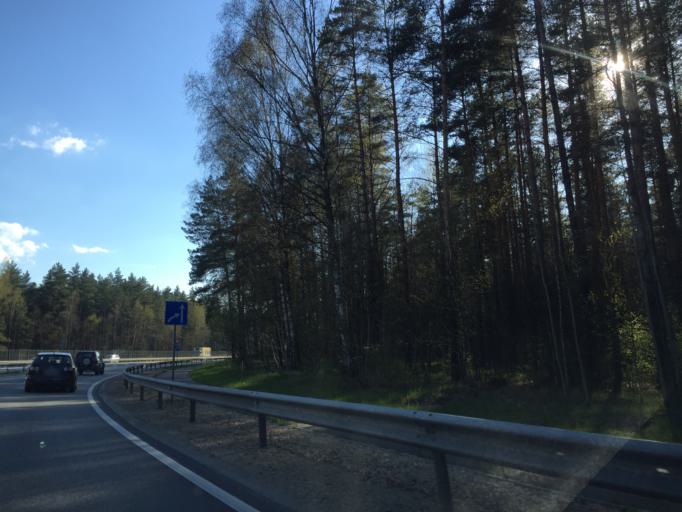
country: LV
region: Riga
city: Bergi
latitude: 57.0096
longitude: 24.3044
